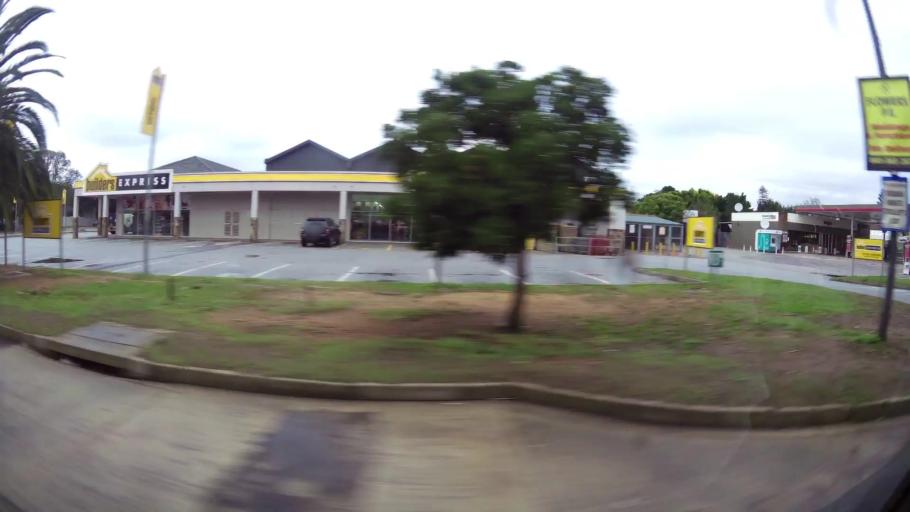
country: ZA
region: Eastern Cape
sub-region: Nelson Mandela Bay Metropolitan Municipality
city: Port Elizabeth
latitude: -33.9782
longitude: 25.5861
